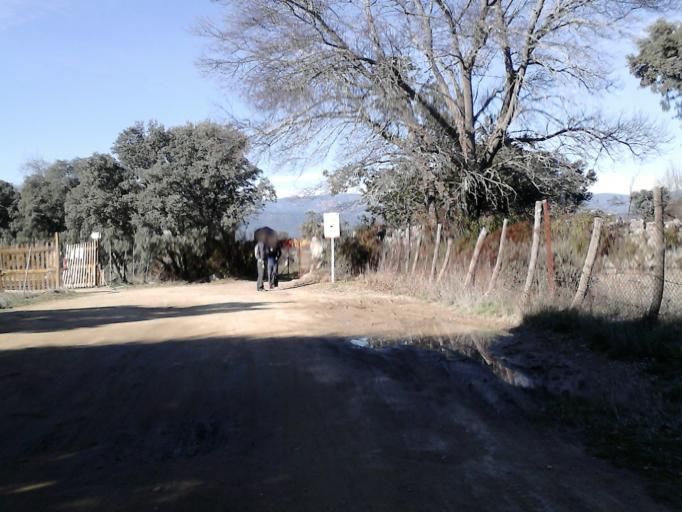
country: ES
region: Madrid
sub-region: Provincia de Madrid
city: Navalquejigo
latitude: 40.6120
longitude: -4.0743
